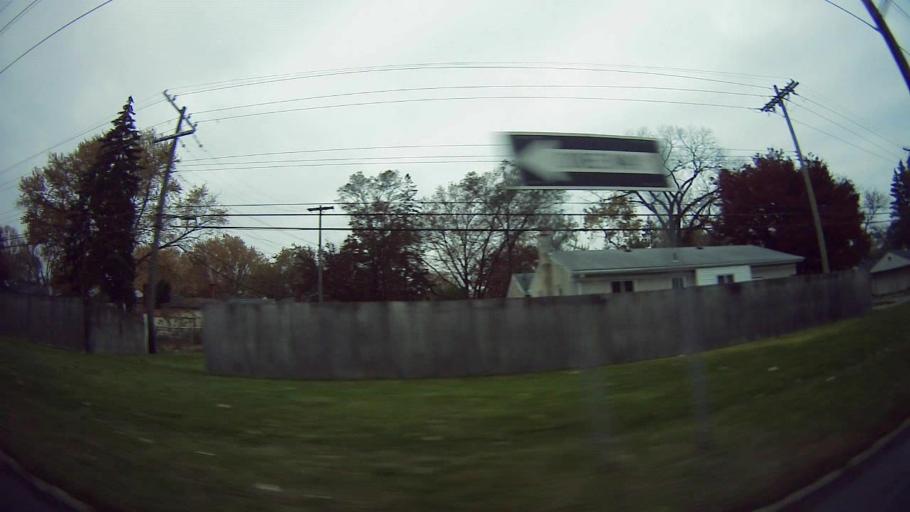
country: US
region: Michigan
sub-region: Wayne County
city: Redford
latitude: 42.4089
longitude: -83.2773
